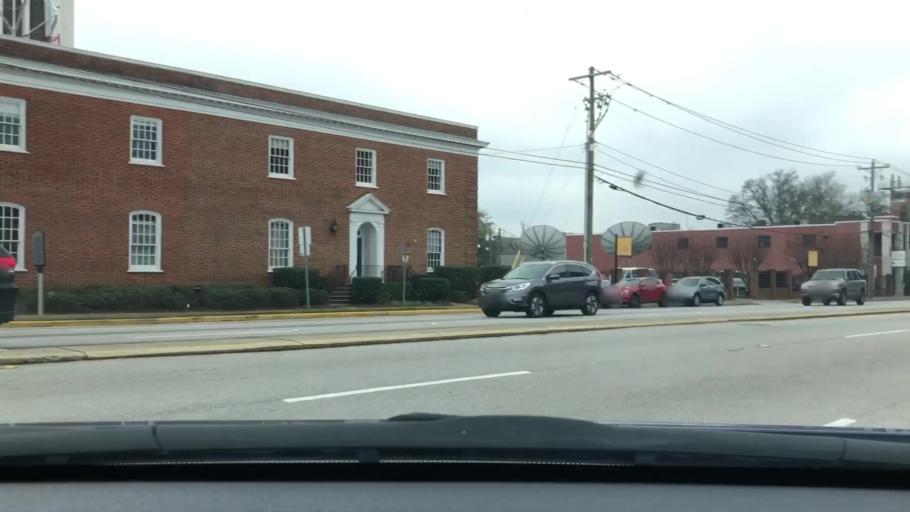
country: US
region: South Carolina
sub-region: Richland County
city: Columbia
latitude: 34.0028
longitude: -81.0290
